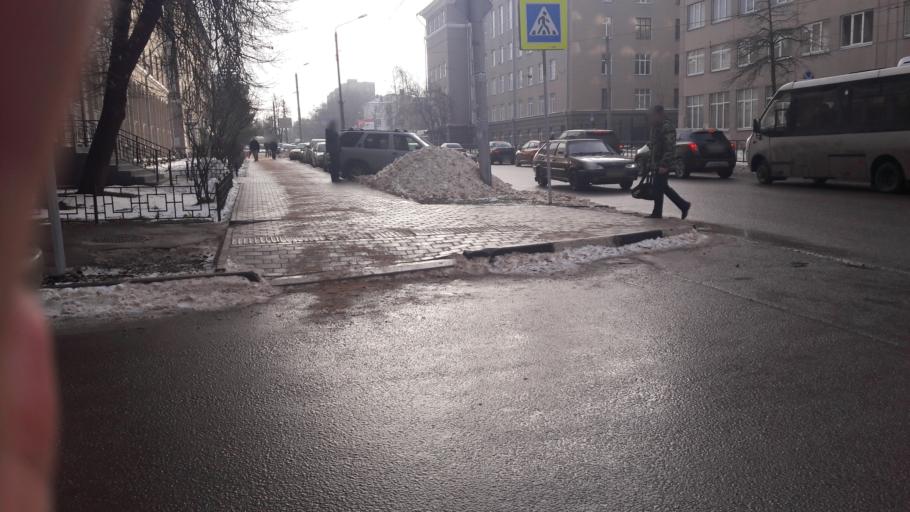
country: RU
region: Tula
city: Mendeleyevskiy
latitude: 54.1679
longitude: 37.5865
